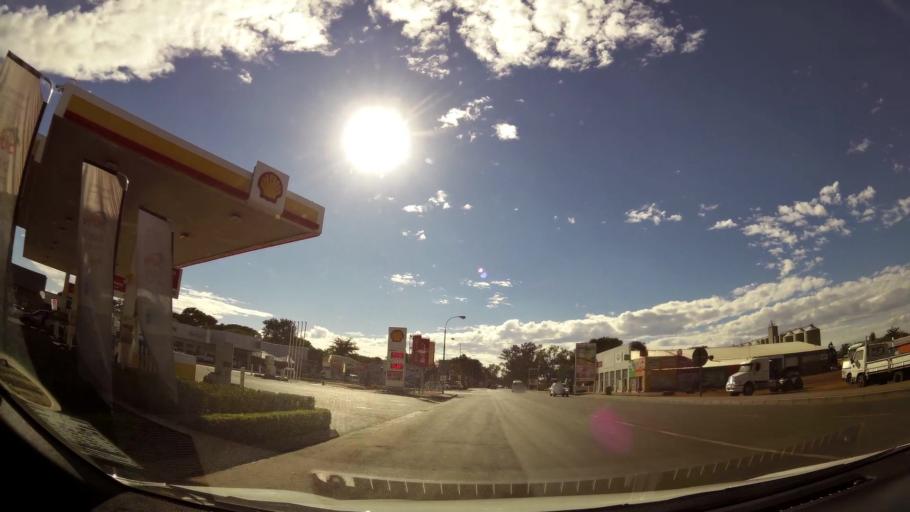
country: ZA
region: Limpopo
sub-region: Waterberg District Municipality
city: Bela-Bela
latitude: -24.8852
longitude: 28.2984
